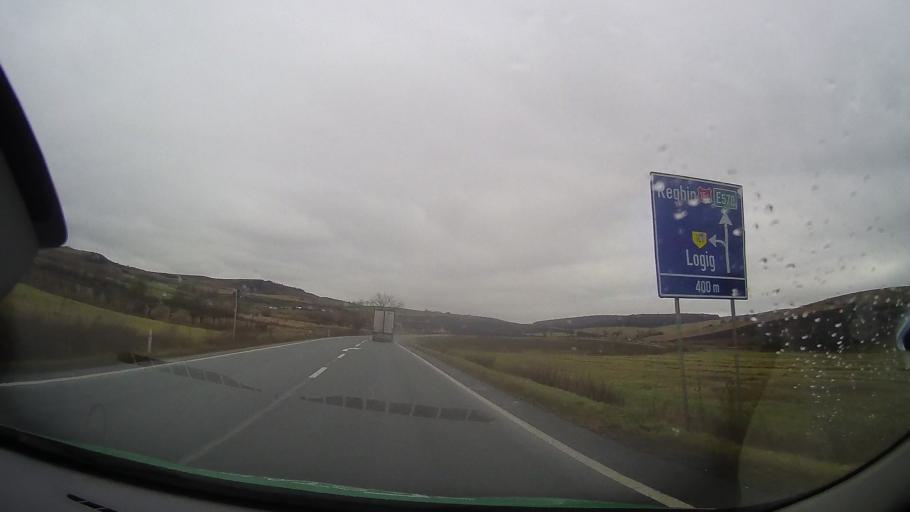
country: RO
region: Mures
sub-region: Comuna Lunca
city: Lunca
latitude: 46.8717
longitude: 24.5507
